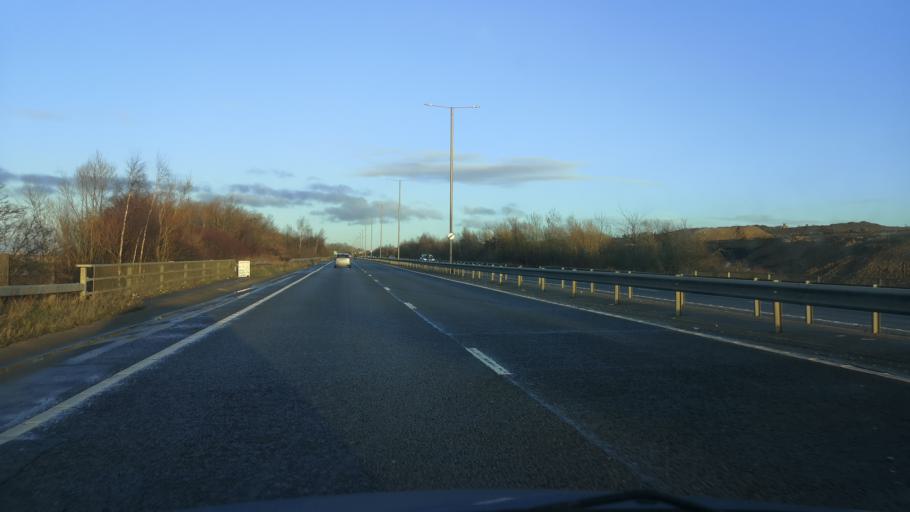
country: GB
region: England
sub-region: Barnsley
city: Birdwell
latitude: 53.5038
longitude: -1.4687
